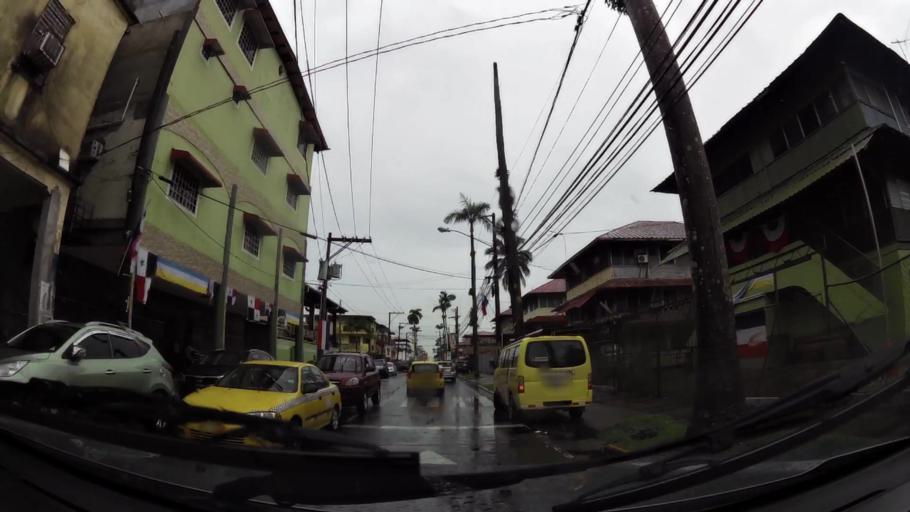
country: PA
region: Colon
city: Colon
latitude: 9.3606
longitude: -79.9003
